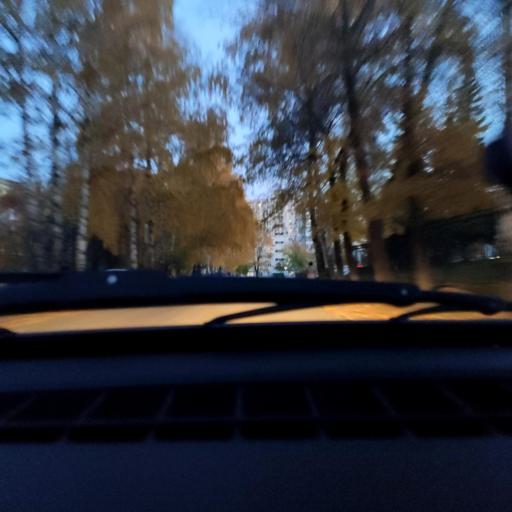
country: RU
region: Bashkortostan
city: Ufa
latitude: 54.8055
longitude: 56.1221
